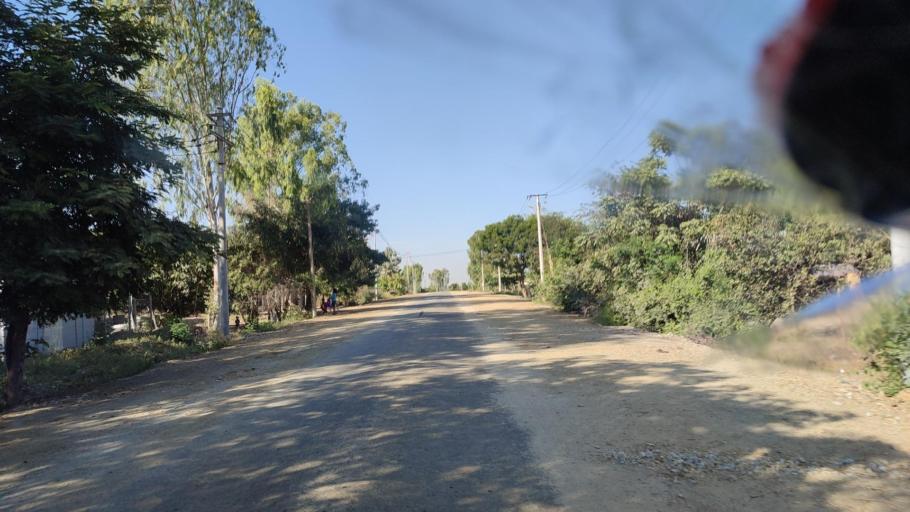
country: MM
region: Mandalay
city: Pyinmana
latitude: 20.0856
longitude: 96.2646
